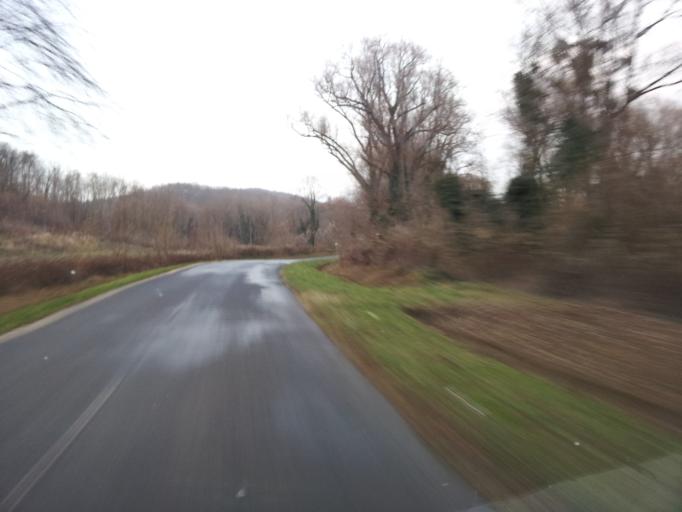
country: HU
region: Zala
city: Zalaszentgrot
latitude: 46.8789
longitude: 17.1479
